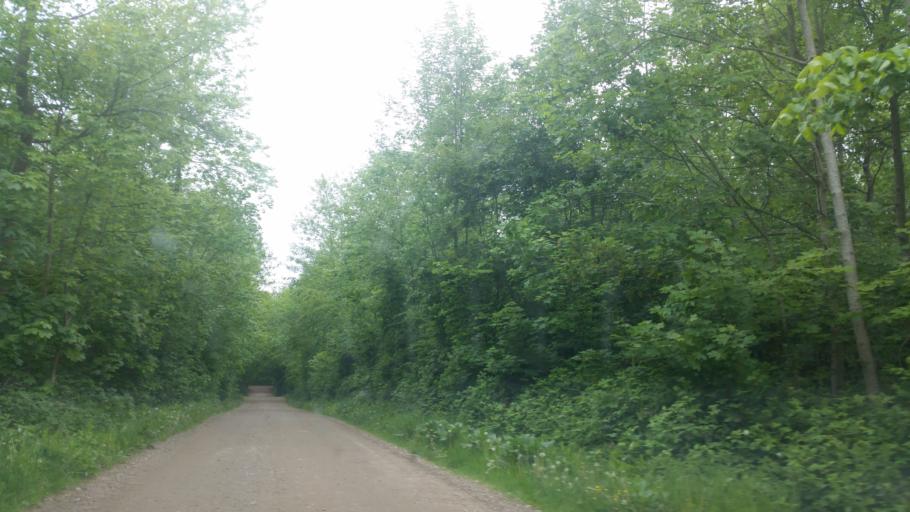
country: DK
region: South Denmark
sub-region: Middelfart Kommune
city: Middelfart
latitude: 55.4952
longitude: 9.7182
